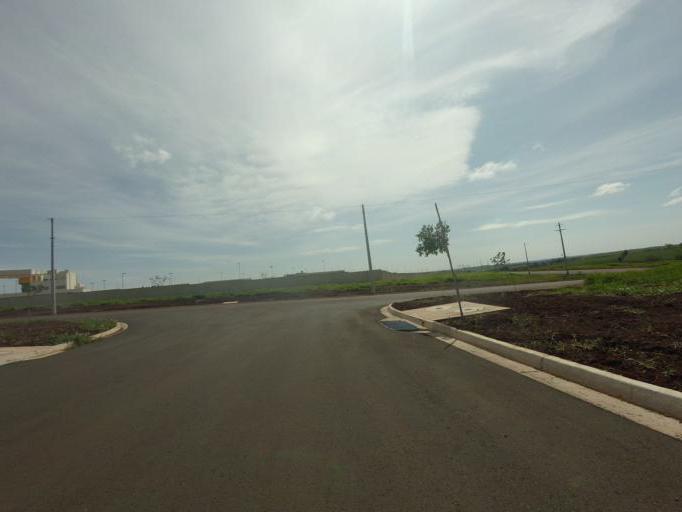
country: BR
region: Sao Paulo
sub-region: Piracicaba
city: Piracicaba
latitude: -22.7635
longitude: -47.5840
